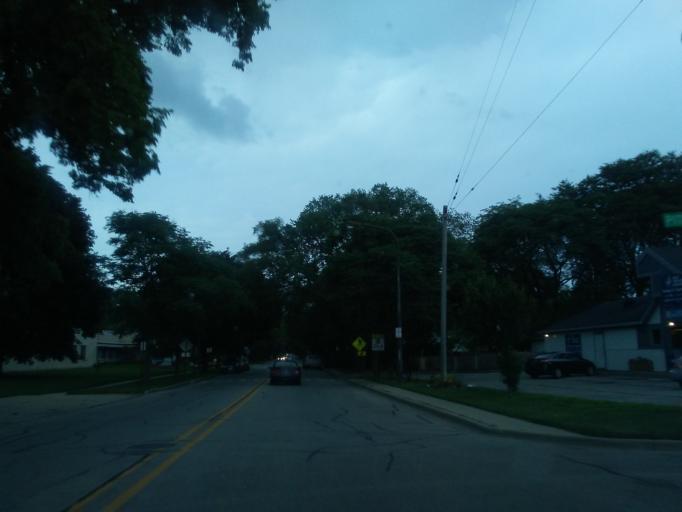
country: US
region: Illinois
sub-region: Cook County
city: Evanston
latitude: 42.0337
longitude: -87.7048
